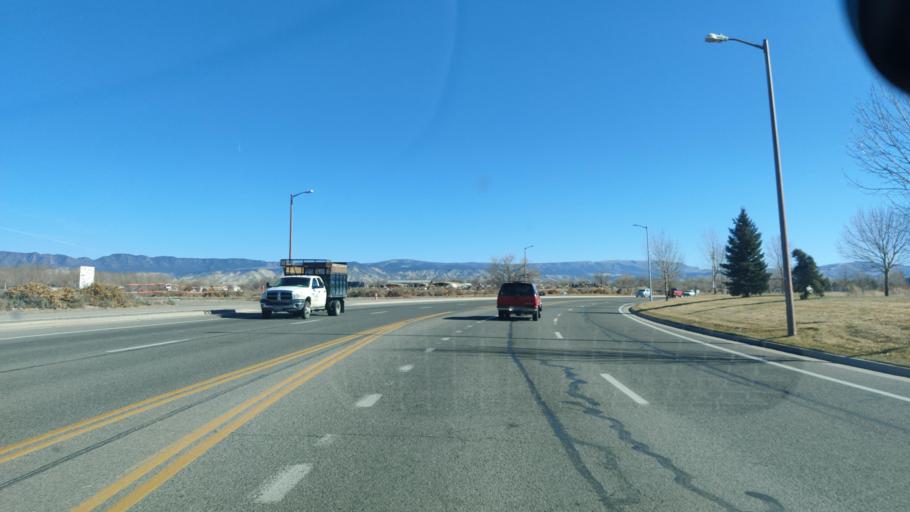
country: US
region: Colorado
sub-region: Montrose County
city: Montrose
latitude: 38.4907
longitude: -107.8790
